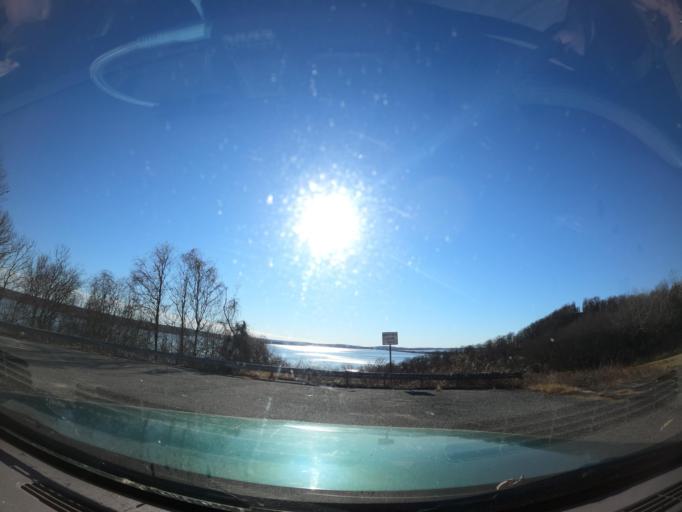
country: US
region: Oklahoma
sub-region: McIntosh County
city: Eufaula
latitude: 35.2502
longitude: -95.5709
